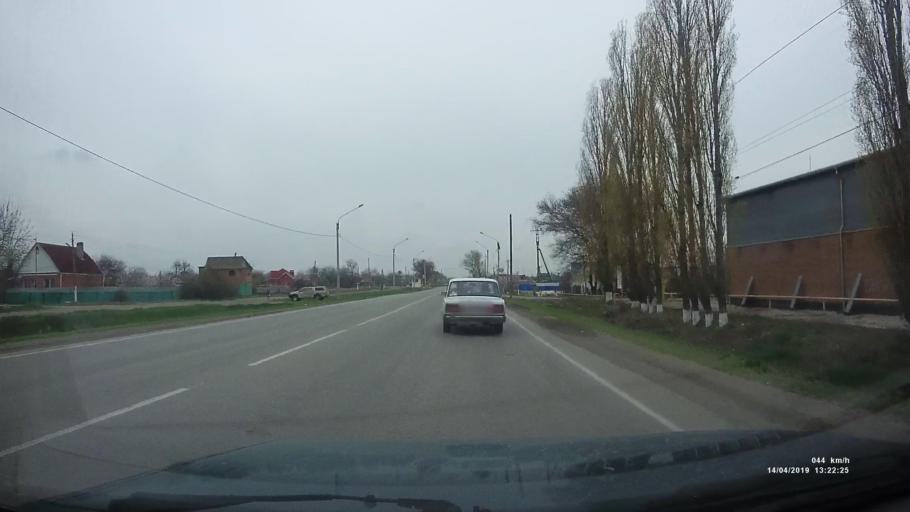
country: RU
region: Rostov
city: Kuleshovka
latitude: 47.0826
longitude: 39.5104
